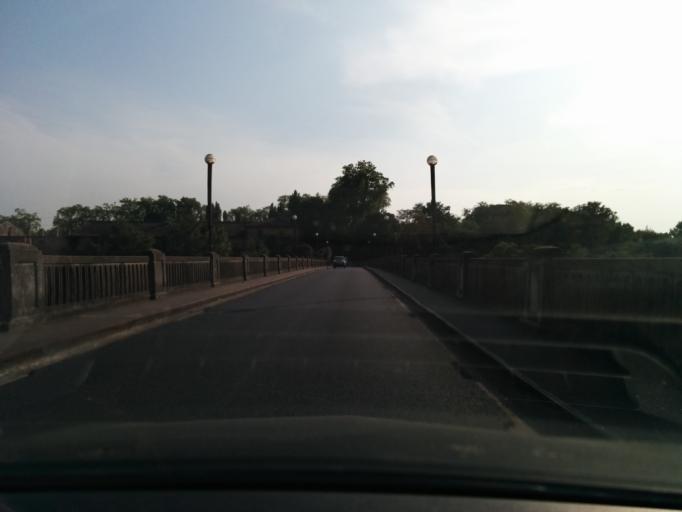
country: FR
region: Midi-Pyrenees
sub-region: Departement du Tarn
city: Gaillac
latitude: 43.8976
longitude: 1.8952
